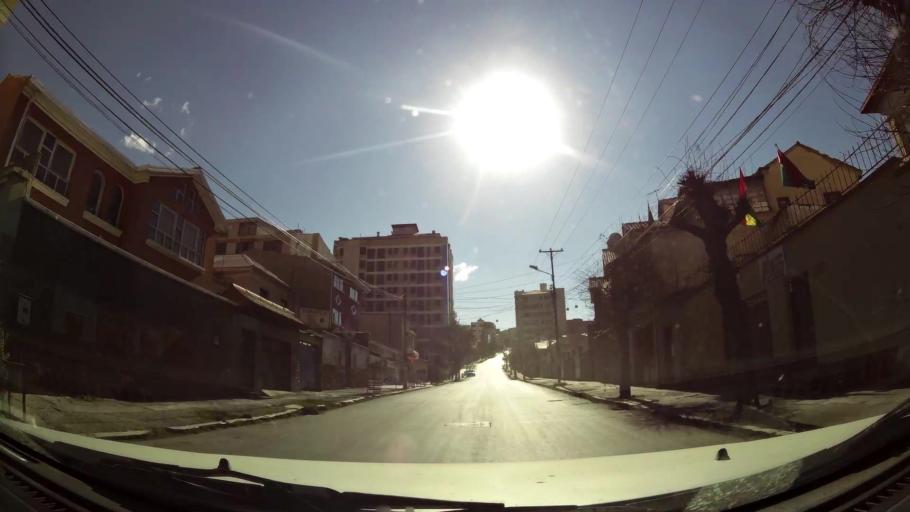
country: BO
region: La Paz
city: La Paz
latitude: -16.5173
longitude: -68.1305
